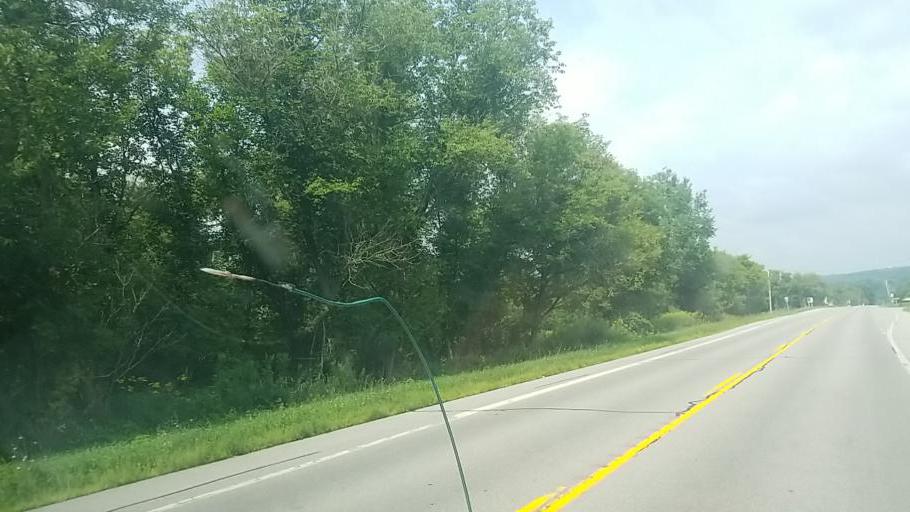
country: US
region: New York
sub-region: Montgomery County
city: Saint Johnsville
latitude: 42.9886
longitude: -74.6517
